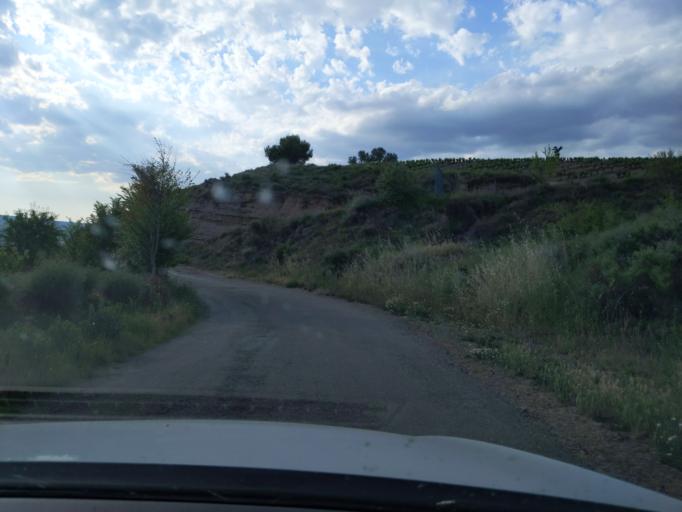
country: ES
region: La Rioja
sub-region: Provincia de La Rioja
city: Albelda de Iregua
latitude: 42.3547
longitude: -2.4646
